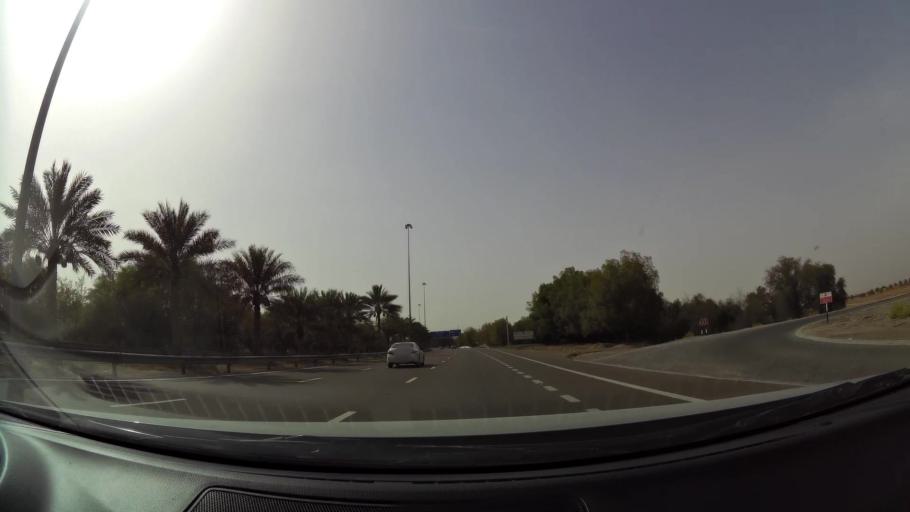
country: AE
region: Abu Dhabi
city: Al Ain
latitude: 24.1939
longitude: 55.5898
